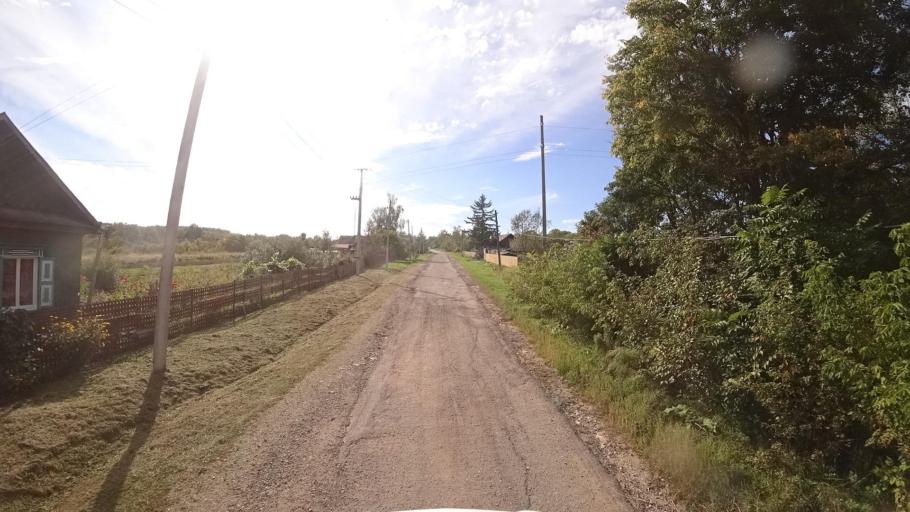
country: RU
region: Primorskiy
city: Dostoyevka
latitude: 44.2968
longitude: 133.4619
